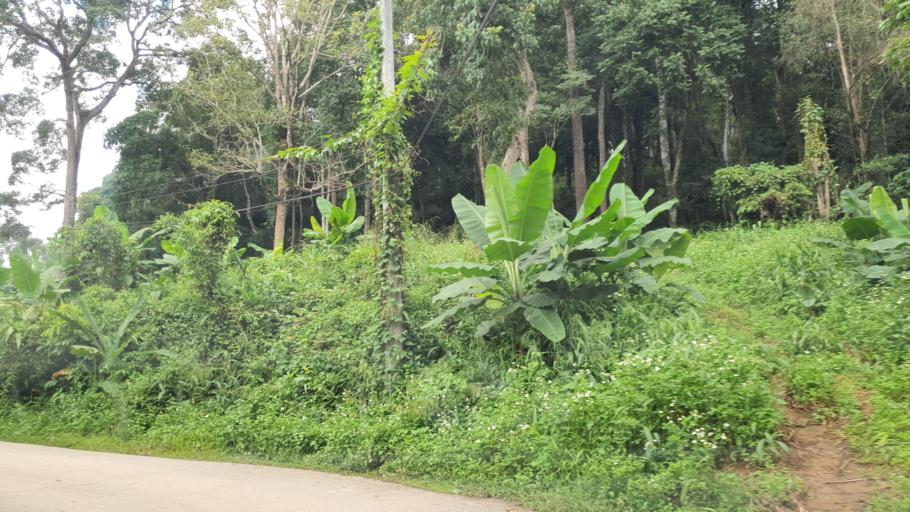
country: TH
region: Chiang Mai
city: Mae On
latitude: 18.9254
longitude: 99.3123
